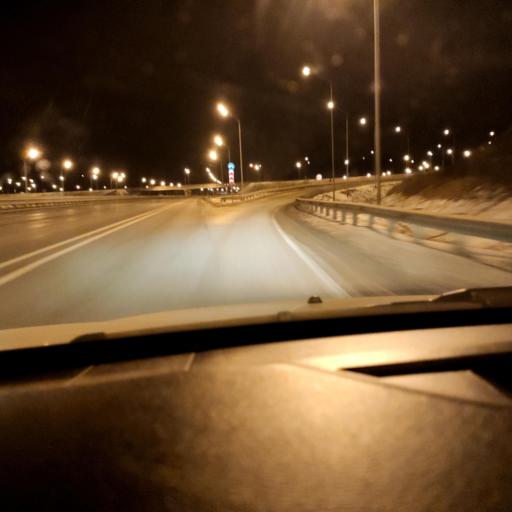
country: RU
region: Samara
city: Smyshlyayevka
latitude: 53.1487
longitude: 50.3873
